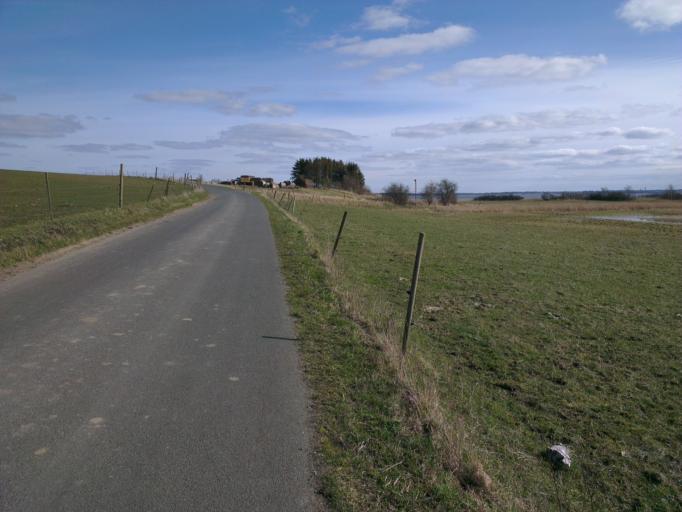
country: DK
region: Zealand
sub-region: Roskilde Kommune
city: Jyllinge
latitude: 55.7354
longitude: 12.0396
